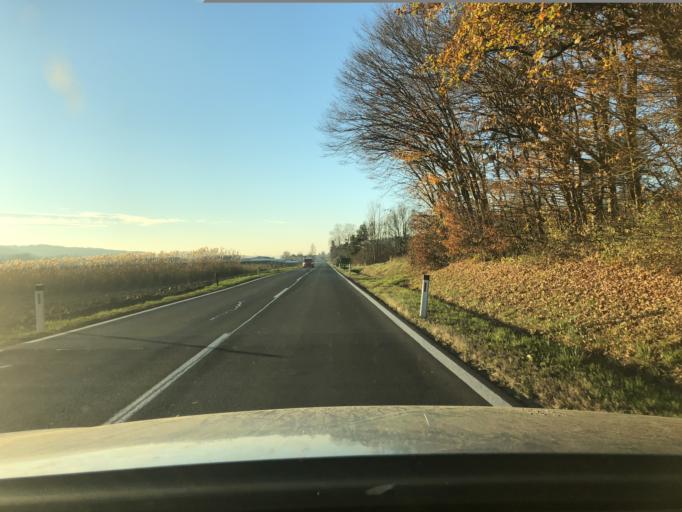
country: AT
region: Styria
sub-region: Politischer Bezirk Hartberg-Fuerstenfeld
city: Ilz
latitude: 47.0893
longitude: 15.8925
